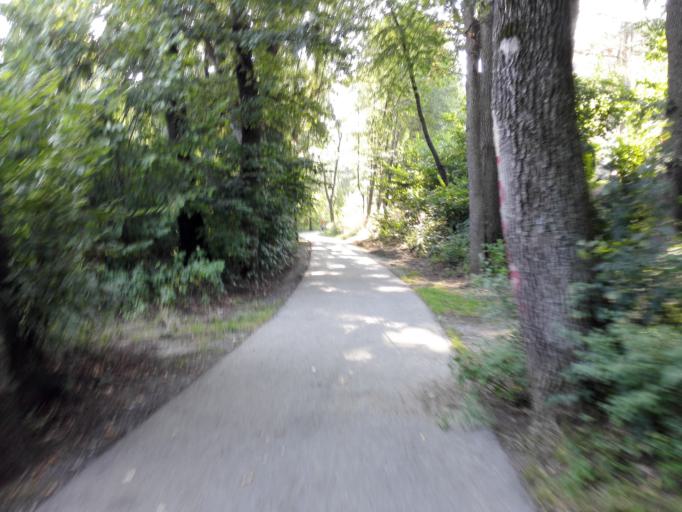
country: AT
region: Styria
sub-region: Graz Stadt
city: Mariatrost
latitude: 47.0765
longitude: 15.4843
